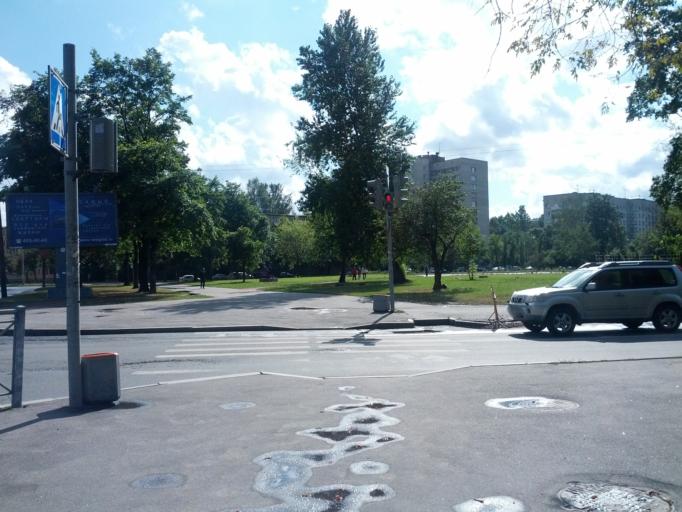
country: RU
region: St.-Petersburg
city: Centralniy
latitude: 59.9337
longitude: 30.4152
